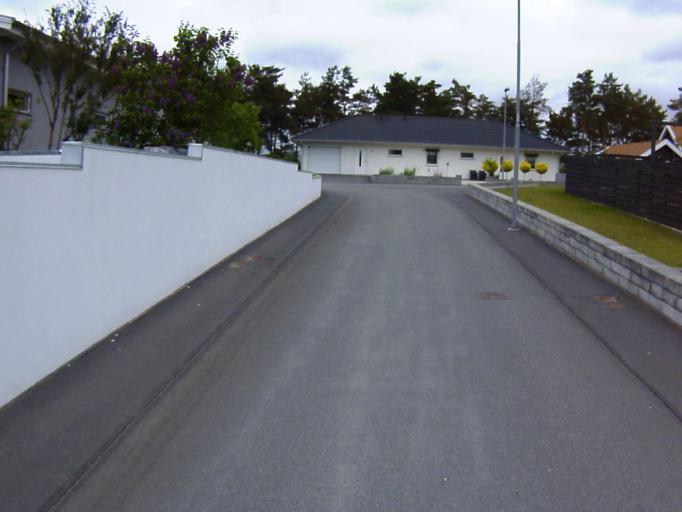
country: SE
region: Skane
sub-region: Kristianstads Kommun
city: Ahus
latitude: 55.9370
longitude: 14.2693
